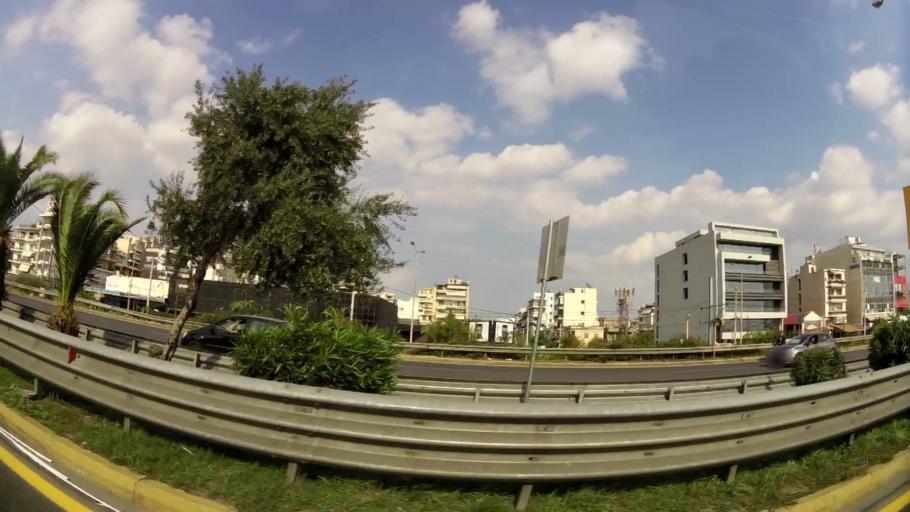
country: GR
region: Attica
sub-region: Nomarchia Athinas
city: Moskhaton
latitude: 37.9413
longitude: 23.6865
